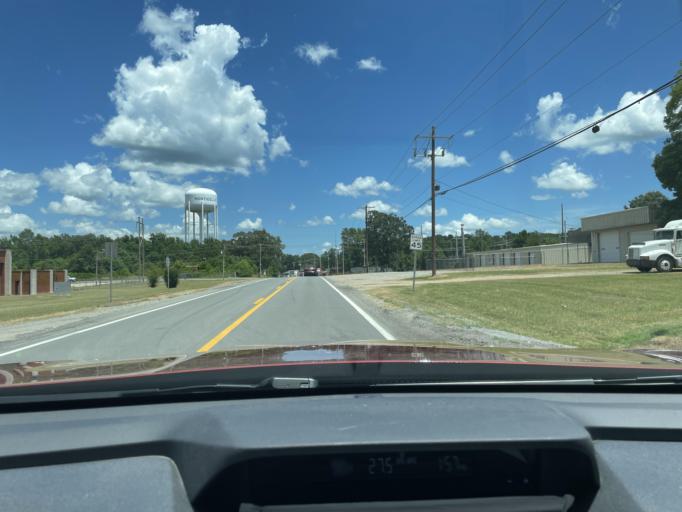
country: US
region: Arkansas
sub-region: Drew County
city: Monticello
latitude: 33.6282
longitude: -91.7699
